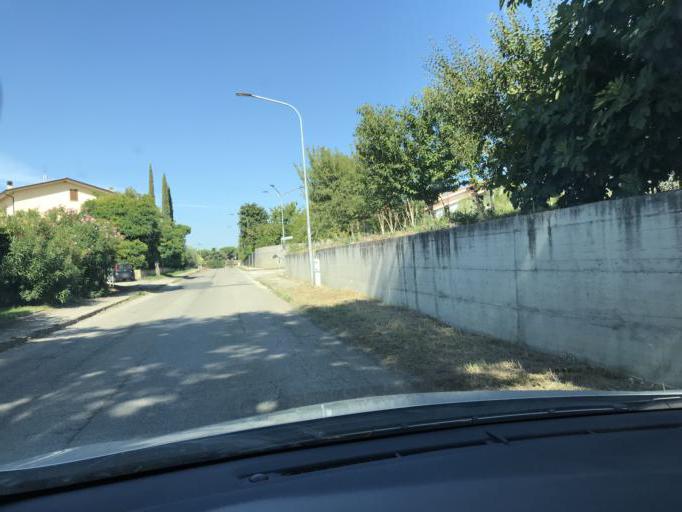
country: IT
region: Umbria
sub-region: Provincia di Perugia
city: Via Lippia
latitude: 43.1069
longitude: 12.4637
